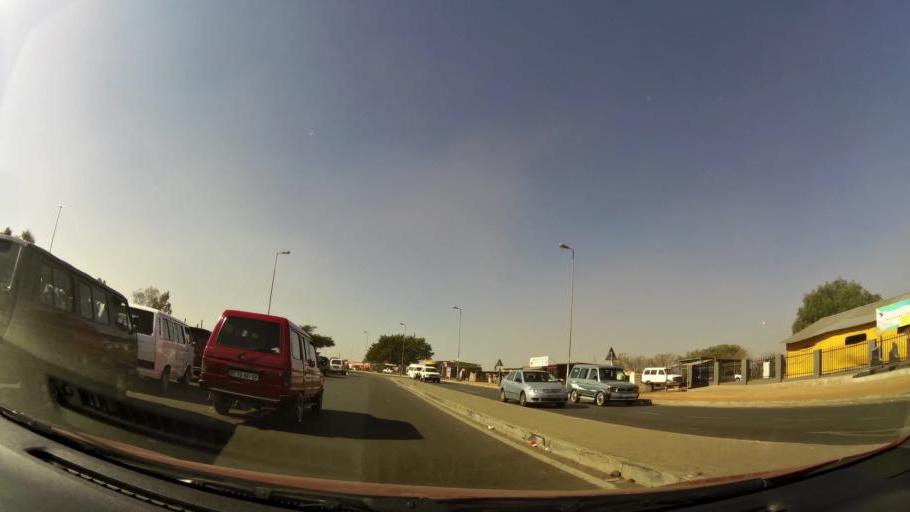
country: ZA
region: Gauteng
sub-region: City of Tshwane Metropolitan Municipality
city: Mabopane
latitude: -25.5504
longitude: 28.0920
